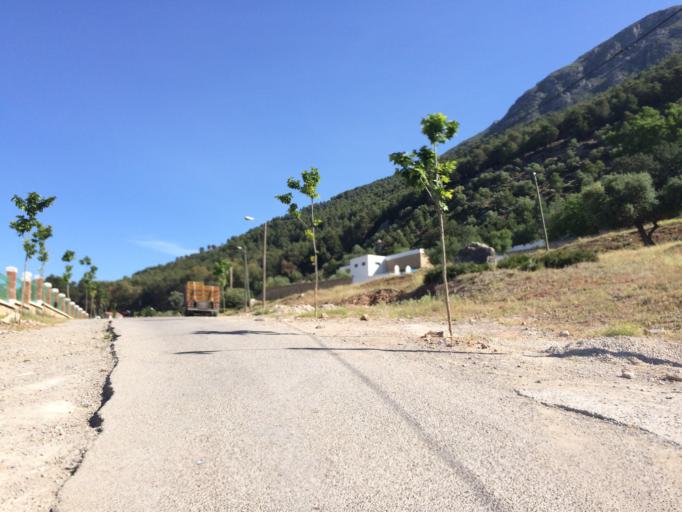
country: MA
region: Tanger-Tetouan
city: Chefchaouene
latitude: 35.1720
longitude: -5.2611
